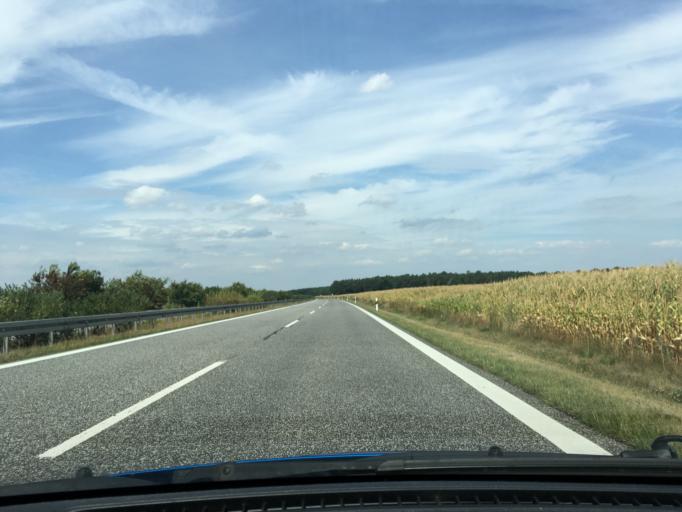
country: DE
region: Mecklenburg-Vorpommern
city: Mirow
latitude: 53.4793
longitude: 11.4892
